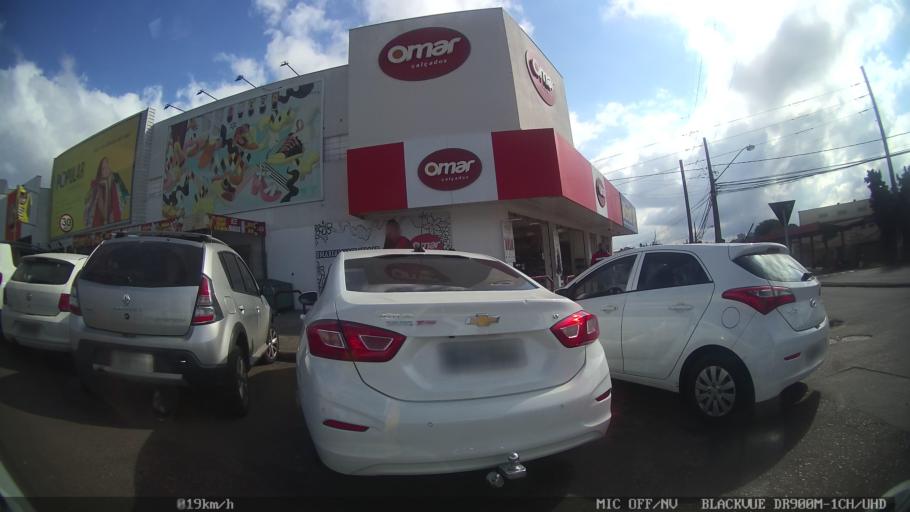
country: BR
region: Parana
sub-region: Pinhais
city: Pinhais
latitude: -25.3679
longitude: -49.1853
